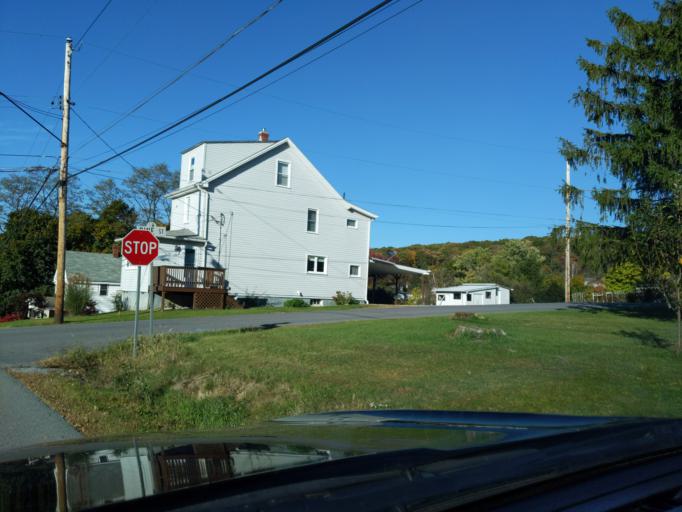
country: US
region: Pennsylvania
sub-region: Blair County
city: Lakemont
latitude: 40.4598
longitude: -78.3926
